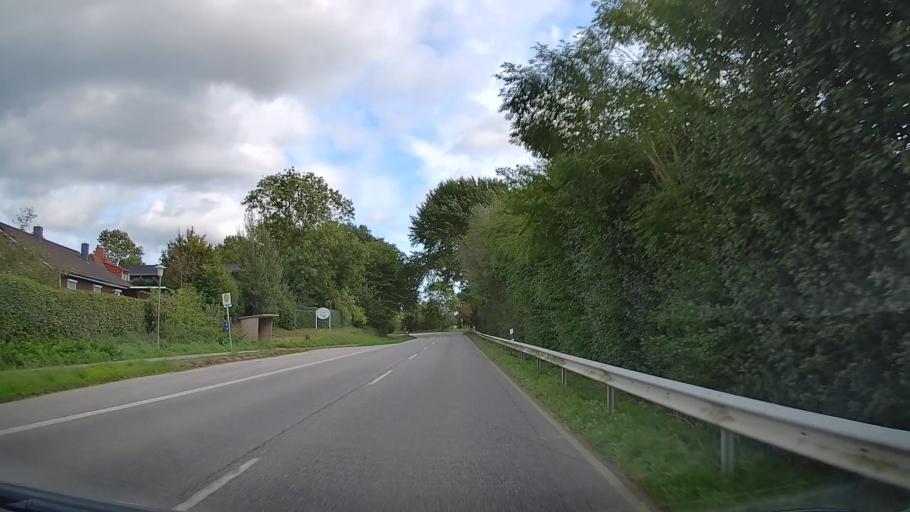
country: DE
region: Schleswig-Holstein
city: Niesgrau
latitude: 54.7500
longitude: 9.8310
